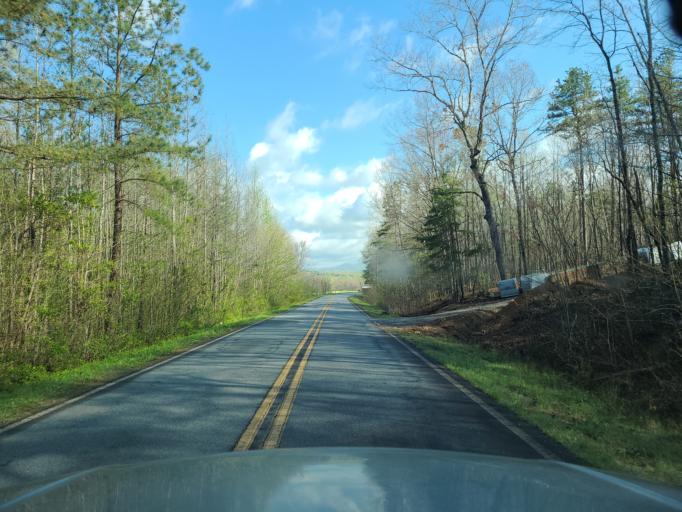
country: US
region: North Carolina
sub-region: Rutherford County
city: Forest City
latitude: 35.4022
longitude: -81.8232
